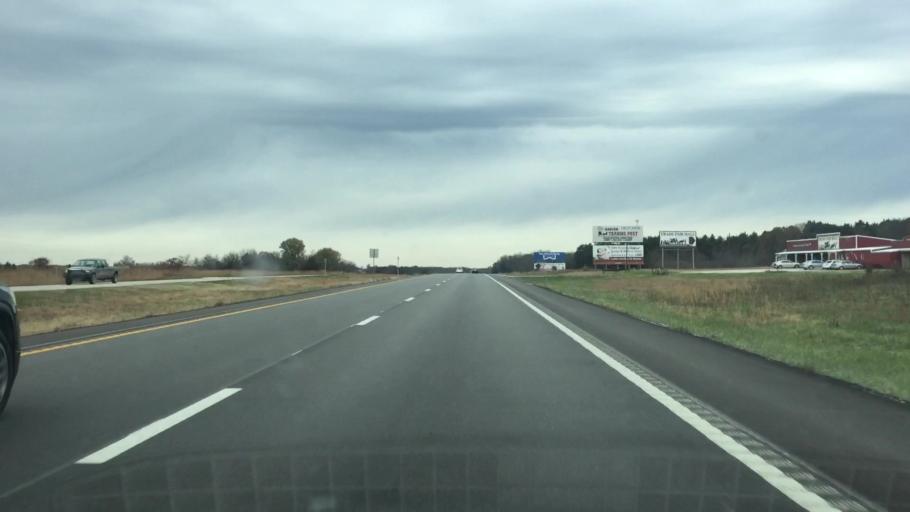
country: US
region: Missouri
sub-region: Saint Clair County
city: Osceola
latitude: 37.9931
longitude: -93.6527
